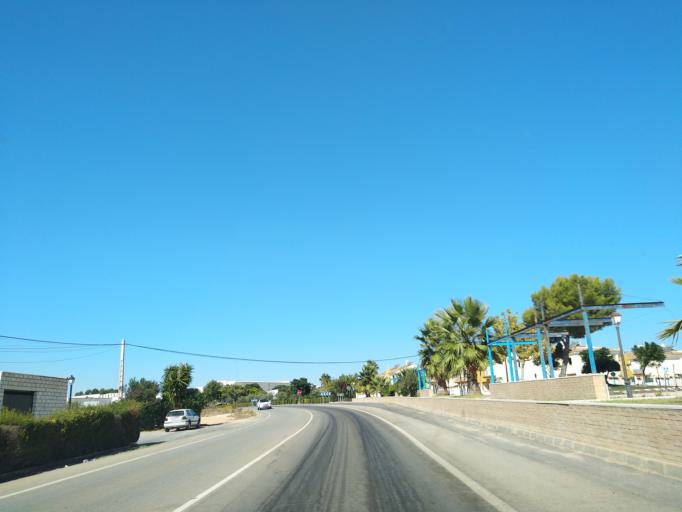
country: ES
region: Andalusia
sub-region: Provincia de Malaga
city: Mollina
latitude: 37.1200
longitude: -4.6607
